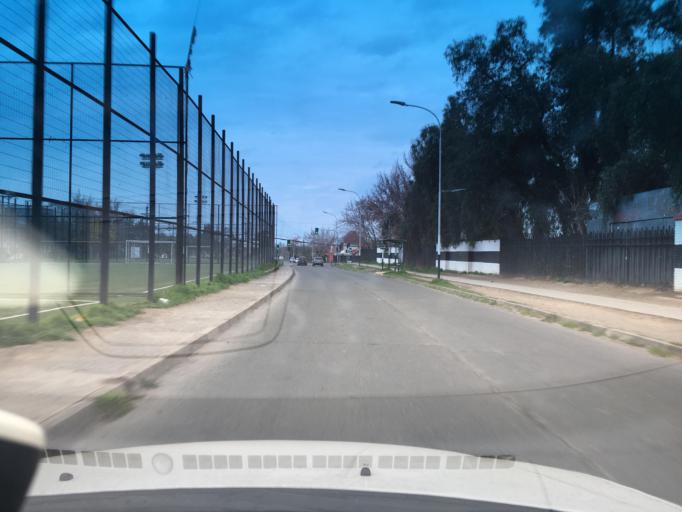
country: CL
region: Santiago Metropolitan
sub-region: Provincia de Santiago
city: Villa Presidente Frei, Nunoa, Santiago, Chile
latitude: -33.5029
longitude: -70.6059
